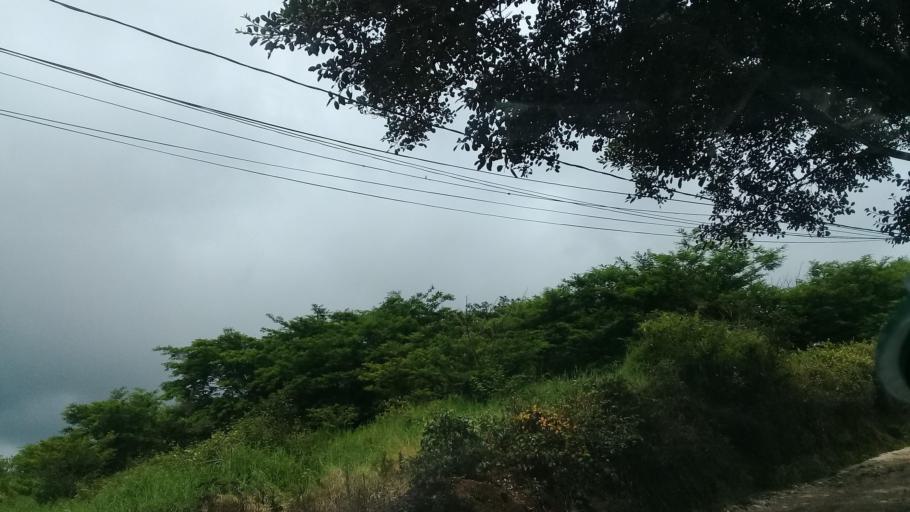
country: MX
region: Veracruz
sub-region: Xalapa
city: Colonia Santa Barbara
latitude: 19.4957
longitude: -96.8712
